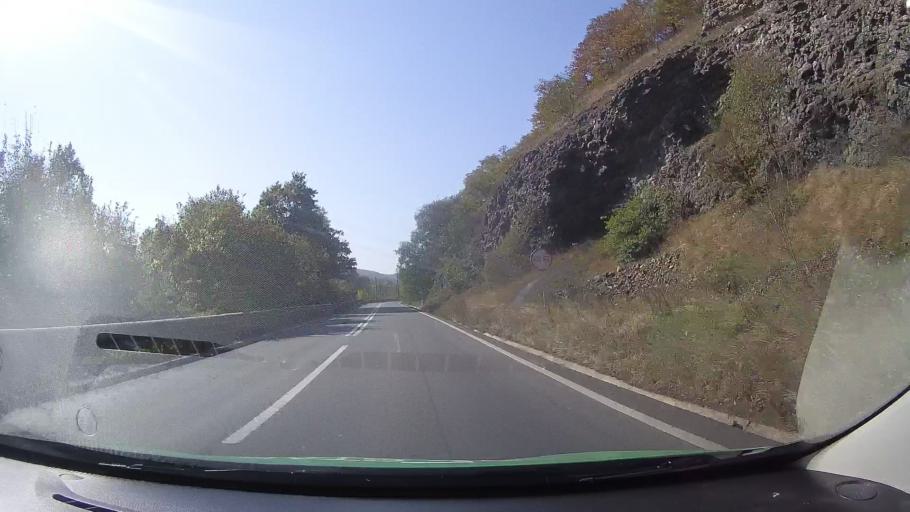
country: RO
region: Arad
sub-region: Comuna Savarsin
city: Savarsin
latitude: 45.9971
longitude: 22.3034
